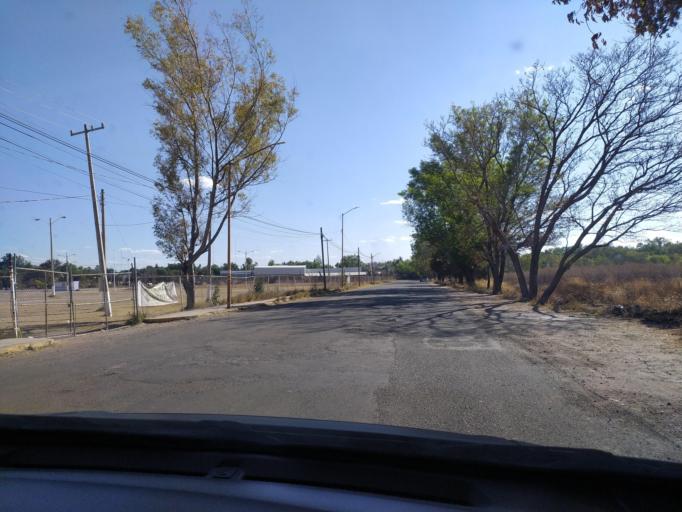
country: LA
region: Oudomxai
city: Muang La
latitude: 21.0303
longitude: 101.8395
